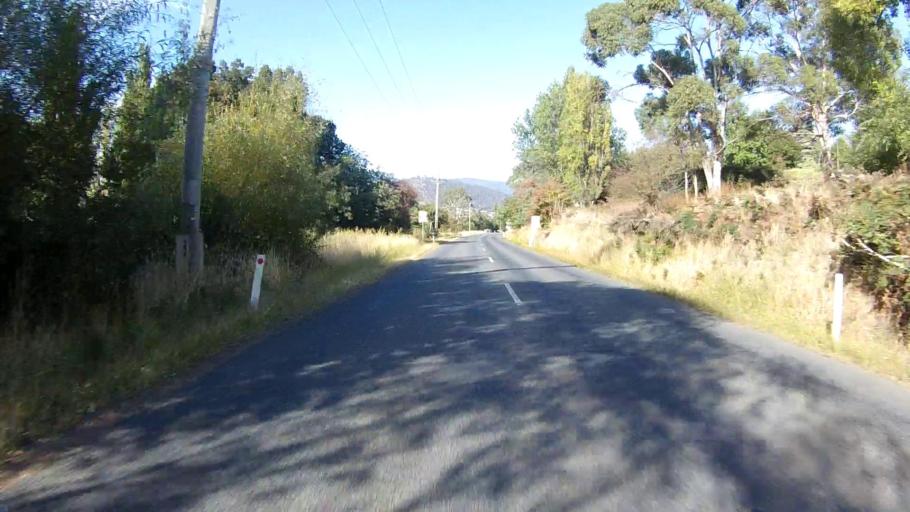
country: AU
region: Tasmania
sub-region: Derwent Valley
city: New Norfolk
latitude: -42.7718
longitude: 147.0670
